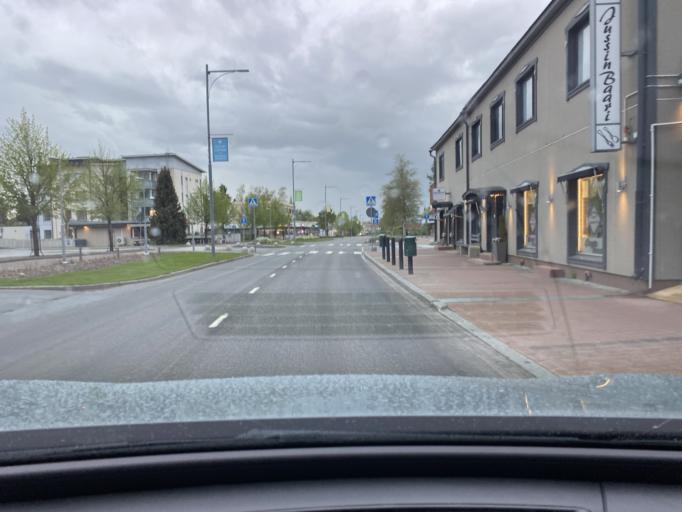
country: FI
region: Varsinais-Suomi
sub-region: Salo
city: Somero
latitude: 60.6305
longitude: 23.5132
